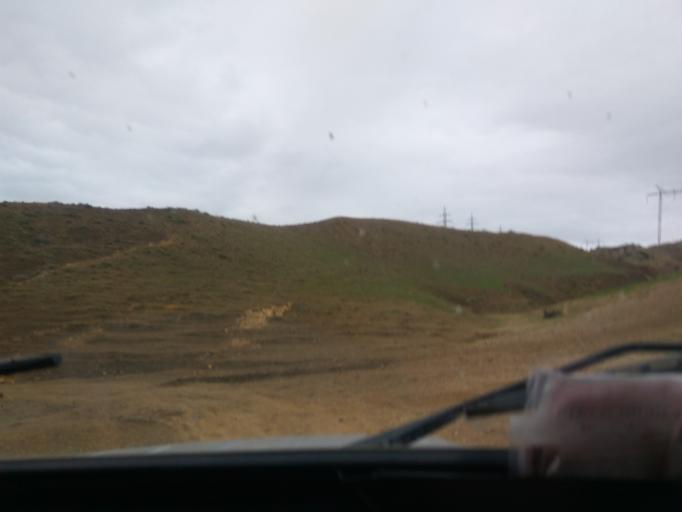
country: RU
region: Dagestan
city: Korkmaskala
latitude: 43.0038
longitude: 47.2129
